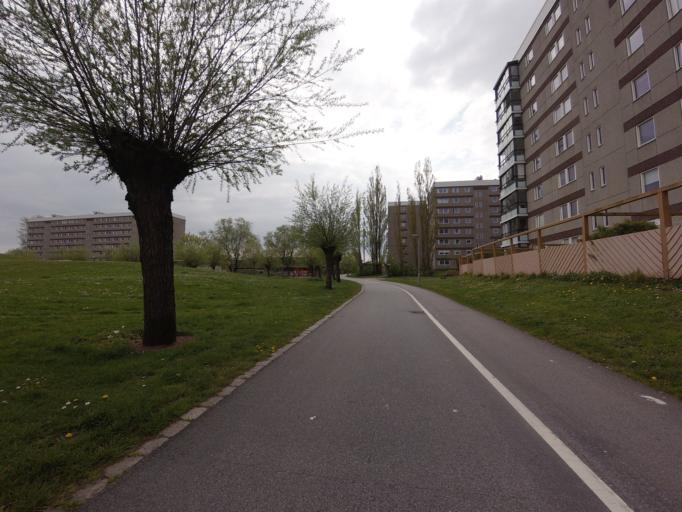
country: SE
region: Skane
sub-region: Malmo
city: Tygelsjo
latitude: 55.5589
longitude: 12.9887
